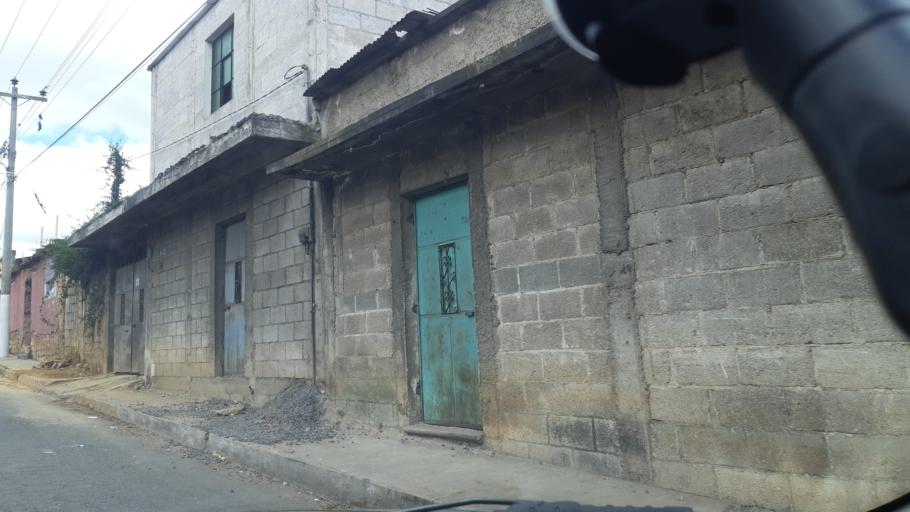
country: GT
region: Chimaltenango
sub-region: Municipio de Chimaltenango
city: Chimaltenango
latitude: 14.6631
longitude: -90.8244
